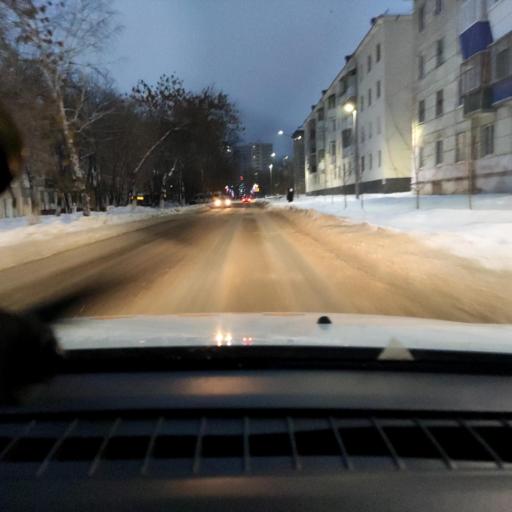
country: RU
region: Samara
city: Novokuybyshevsk
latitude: 53.0968
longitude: 49.9550
